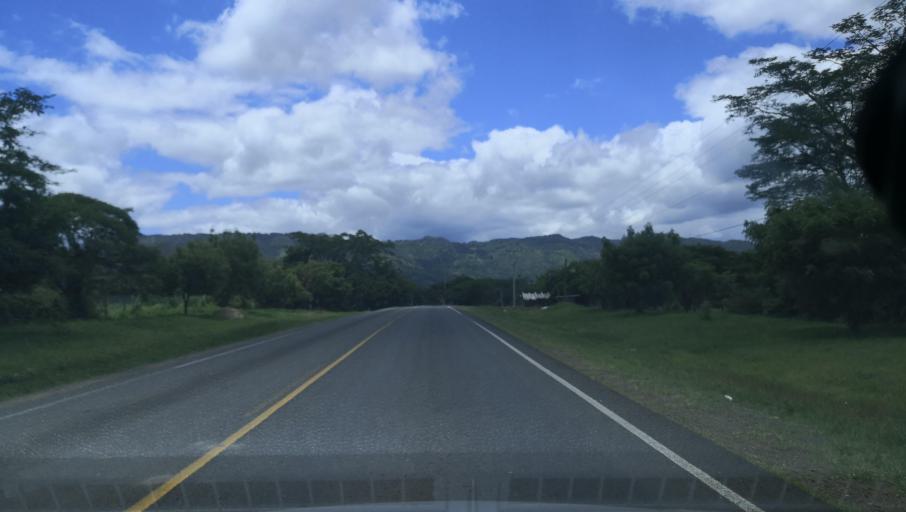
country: NI
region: Esteli
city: Condega
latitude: 13.2494
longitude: -86.3661
